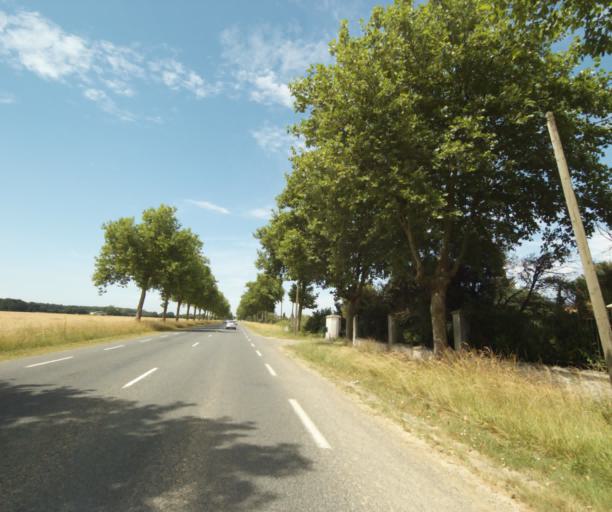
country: FR
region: Ile-de-France
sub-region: Departement de Seine-et-Marne
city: Chailly-en-Biere
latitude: 48.4756
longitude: 2.5995
